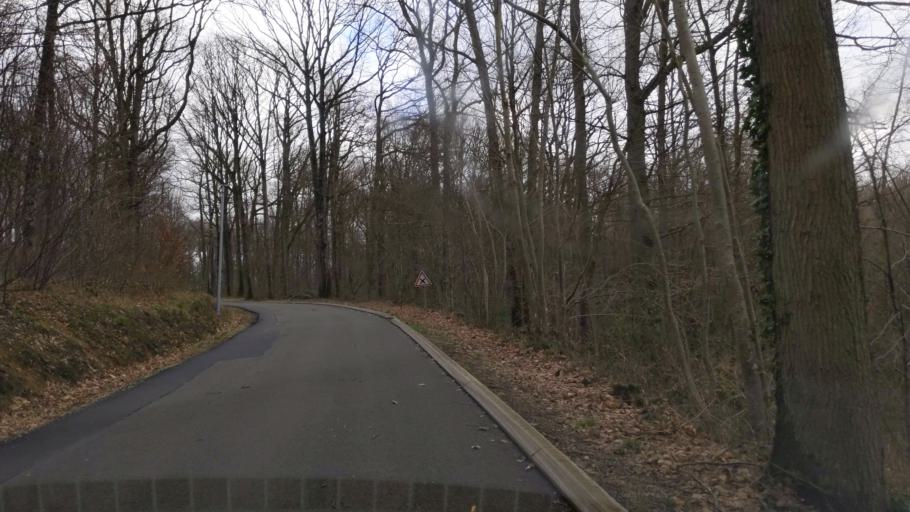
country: FR
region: Ile-de-France
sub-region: Departement des Yvelines
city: Chevreuse
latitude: 48.6947
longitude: 2.0337
